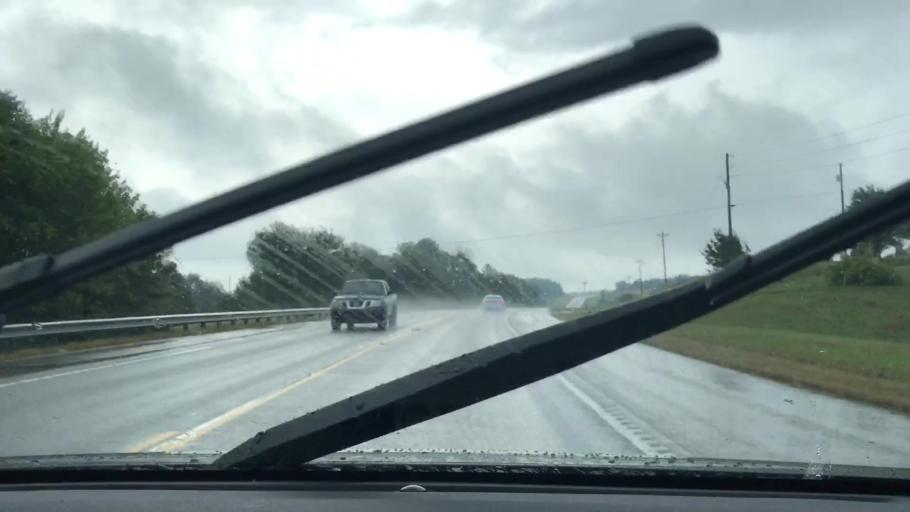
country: US
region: Tennessee
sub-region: Sumner County
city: Westmoreland
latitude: 36.5246
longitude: -86.1595
